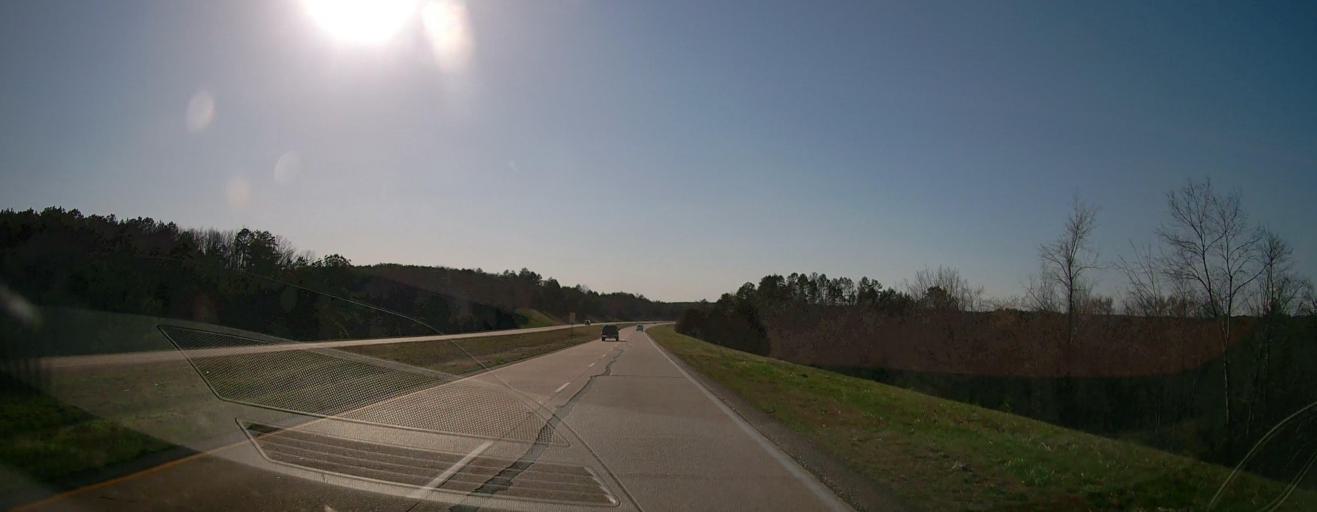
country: US
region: Mississippi
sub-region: Tishomingo County
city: Iuka
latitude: 34.7688
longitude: -88.1295
